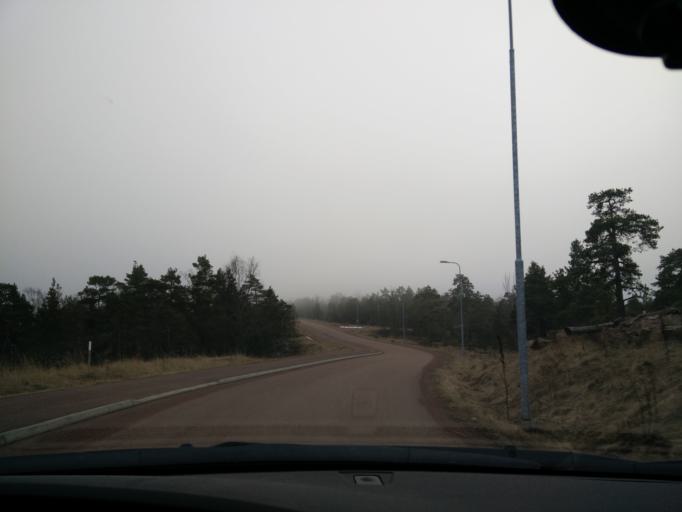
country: AX
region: Alands landsbygd
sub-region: Jomala
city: Jomala
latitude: 60.1297
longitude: 19.9283
